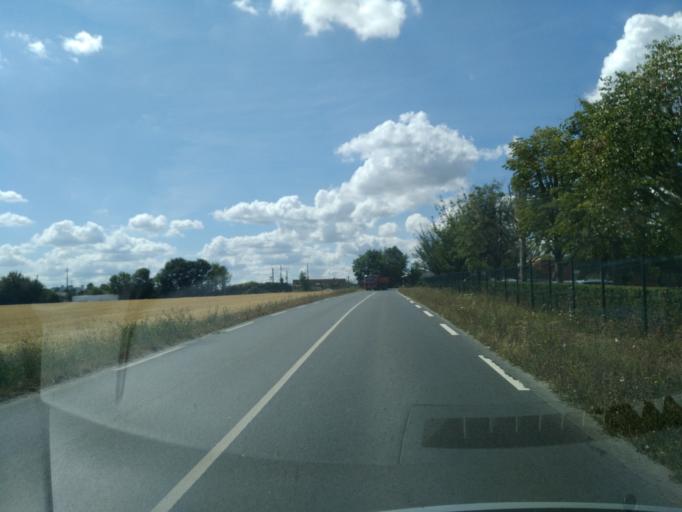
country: FR
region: Ile-de-France
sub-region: Departement des Yvelines
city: Thiverval-Grignon
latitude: 48.8343
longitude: 1.9332
